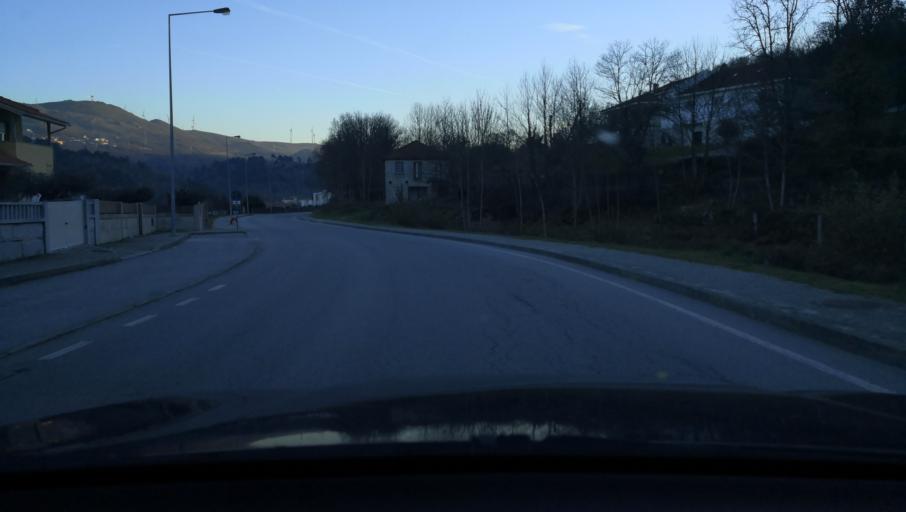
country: PT
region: Vila Real
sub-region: Vila Pouca de Aguiar
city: Vila Pouca de Aguiar
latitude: 41.4946
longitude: -7.6499
